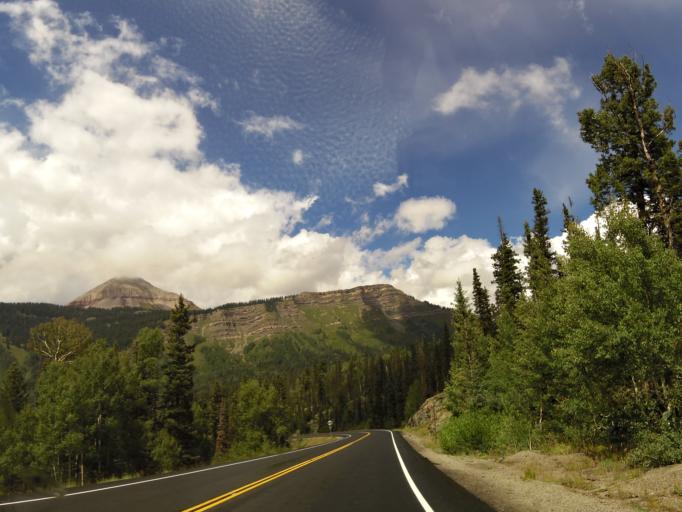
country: US
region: Colorado
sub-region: San Juan County
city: Silverton
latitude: 37.6757
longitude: -107.7819
